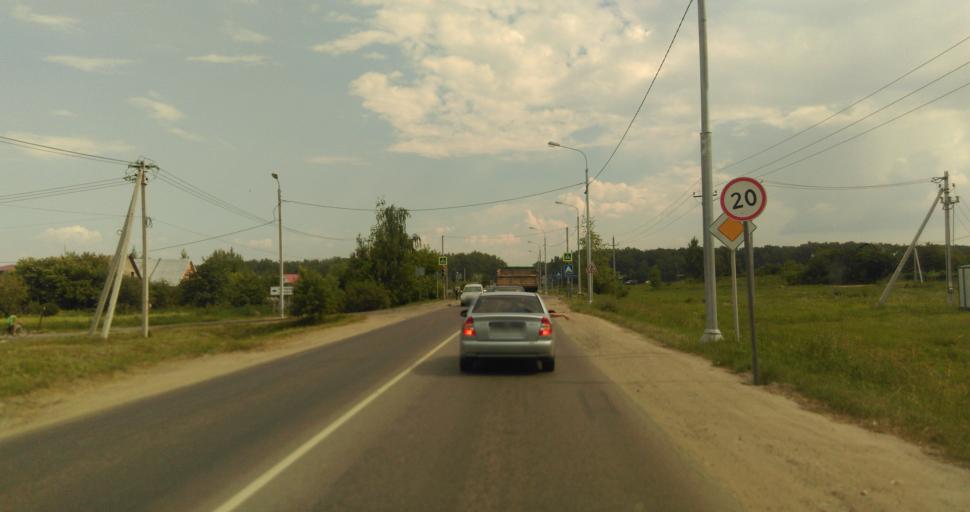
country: RU
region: Moskovskaya
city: Zhitnevo
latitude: 55.3402
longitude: 37.9074
